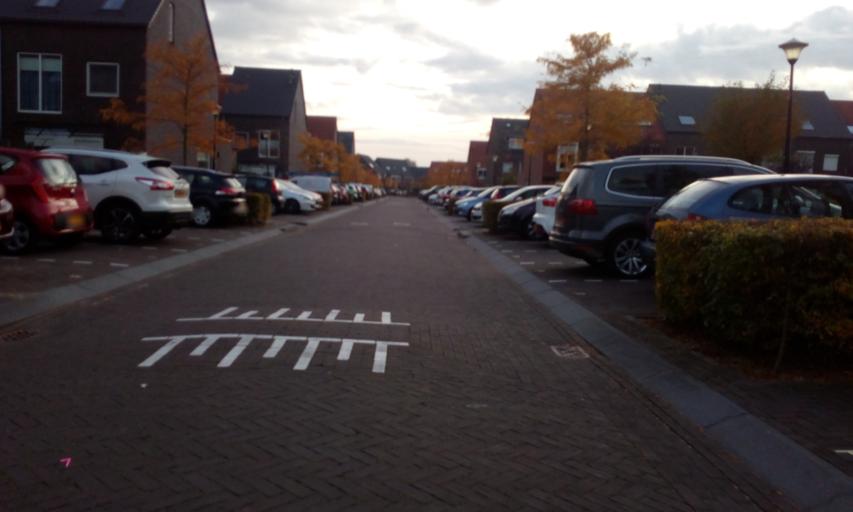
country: NL
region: South Holland
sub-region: Gemeente Lansingerland
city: Berkel en Rodenrijs
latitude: 51.9848
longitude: 4.4728
